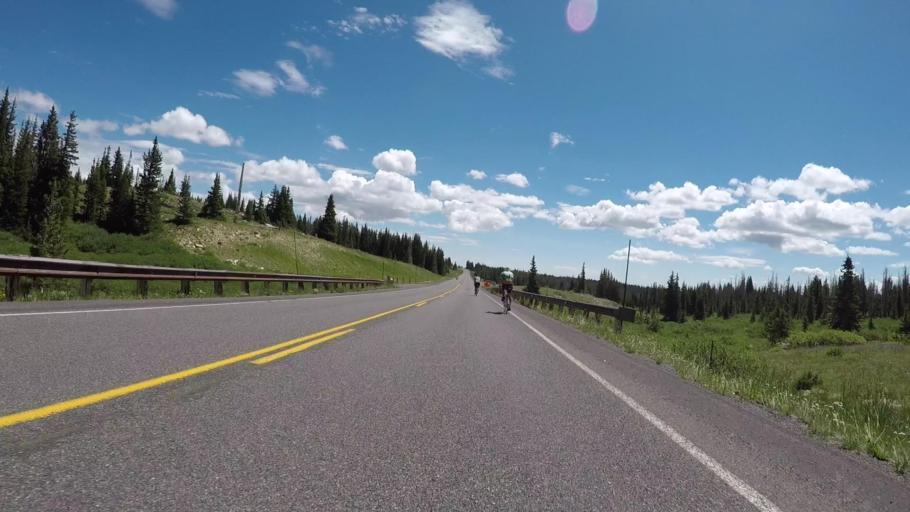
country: US
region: Wyoming
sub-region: Carbon County
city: Saratoga
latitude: 41.3511
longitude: -106.2833
